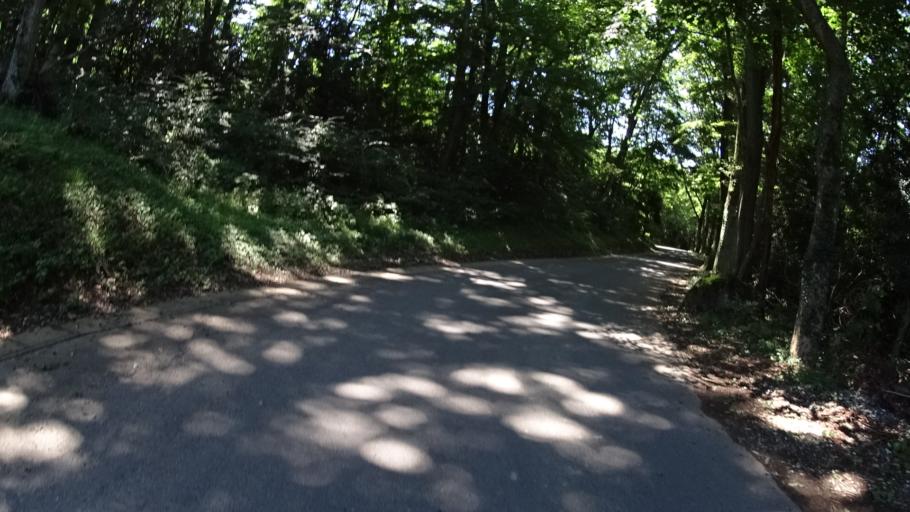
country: JP
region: Iwate
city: Ofunato
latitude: 38.8716
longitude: 141.6116
